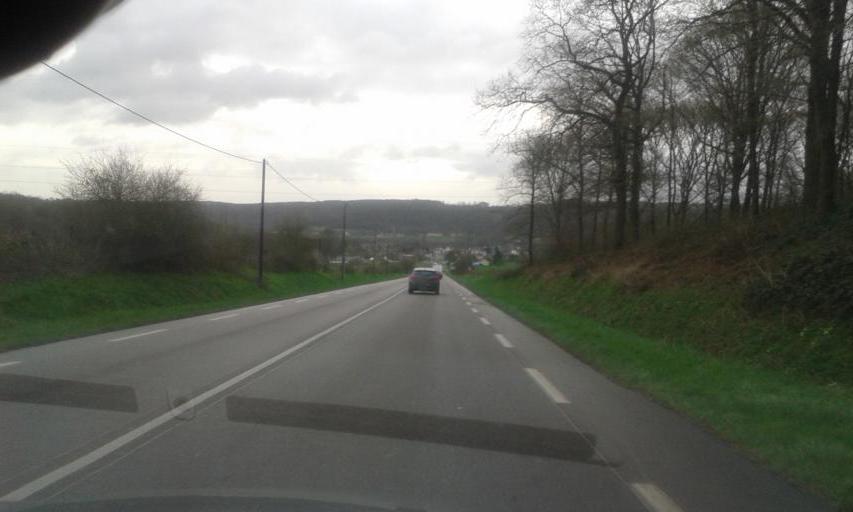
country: FR
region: Haute-Normandie
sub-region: Departement de l'Eure
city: Fleury-sur-Andelle
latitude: 49.3703
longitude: 1.3391
